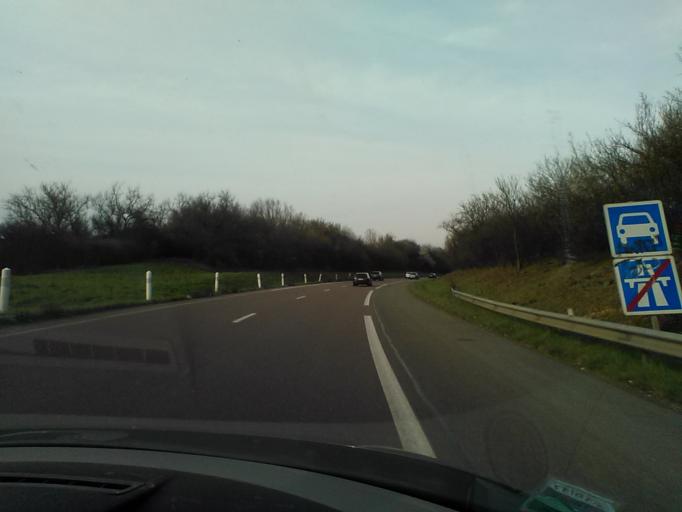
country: FR
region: Ile-de-France
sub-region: Departement de Seine-et-Marne
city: Lieusaint
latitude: 48.6290
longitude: 2.5375
